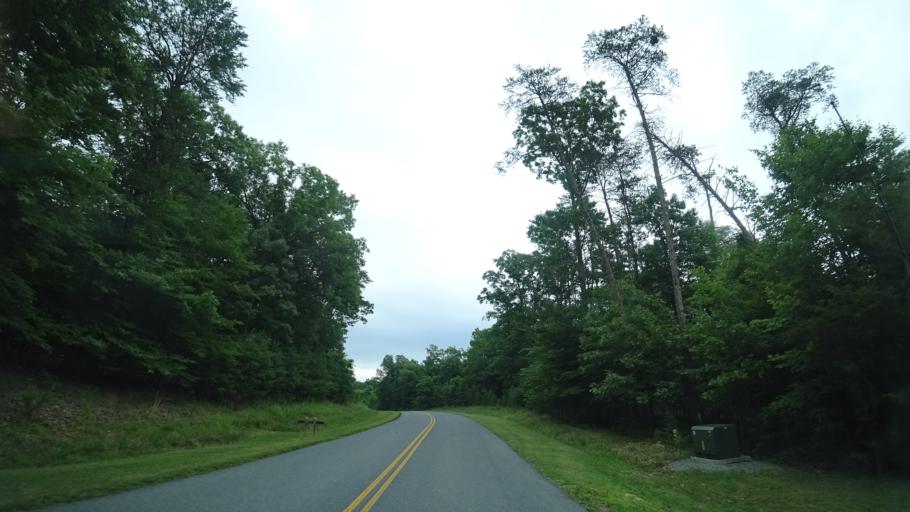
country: US
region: Virginia
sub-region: Warren County
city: Front Royal
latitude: 38.8479
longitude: -78.3062
